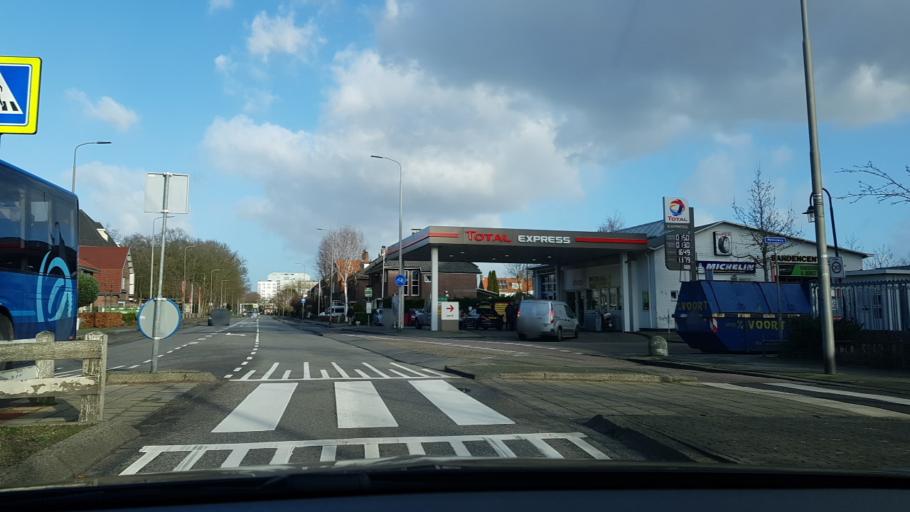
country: NL
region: South Holland
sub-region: Gemeente Teylingen
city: Sassenheim
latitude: 52.2229
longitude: 4.5235
